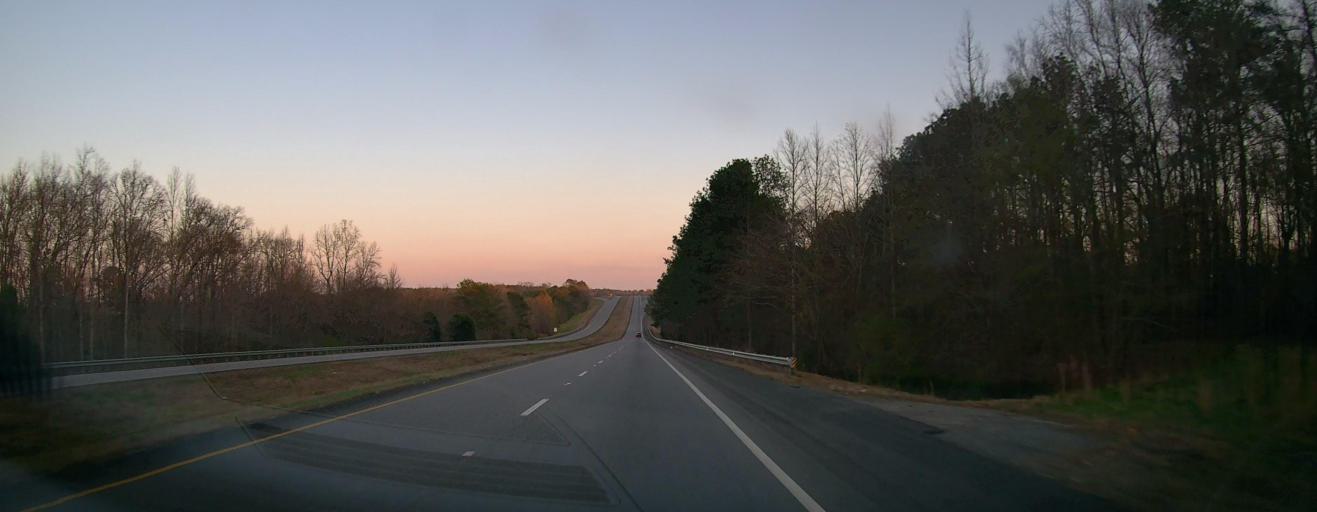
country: US
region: Alabama
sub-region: Coosa County
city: Goodwater
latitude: 32.9937
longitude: -86.0749
